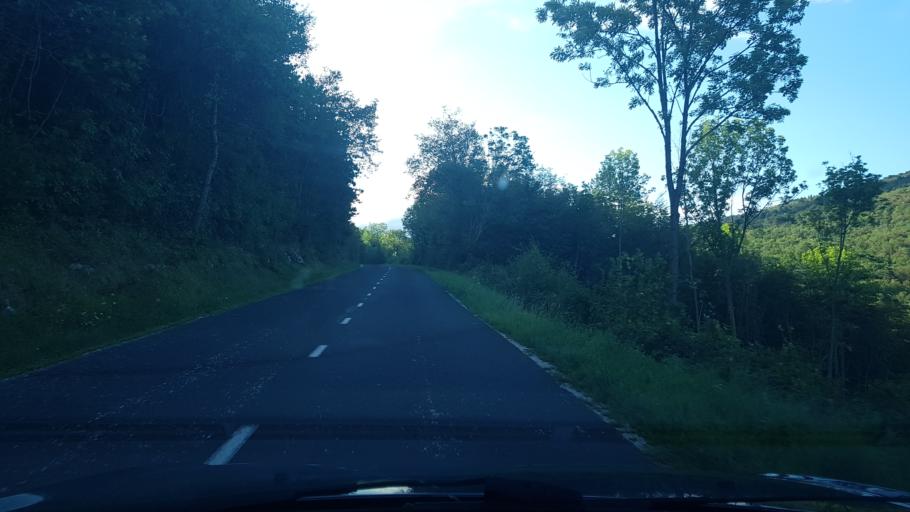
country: SI
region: Nova Gorica
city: Solkan
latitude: 46.0172
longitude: 13.6811
